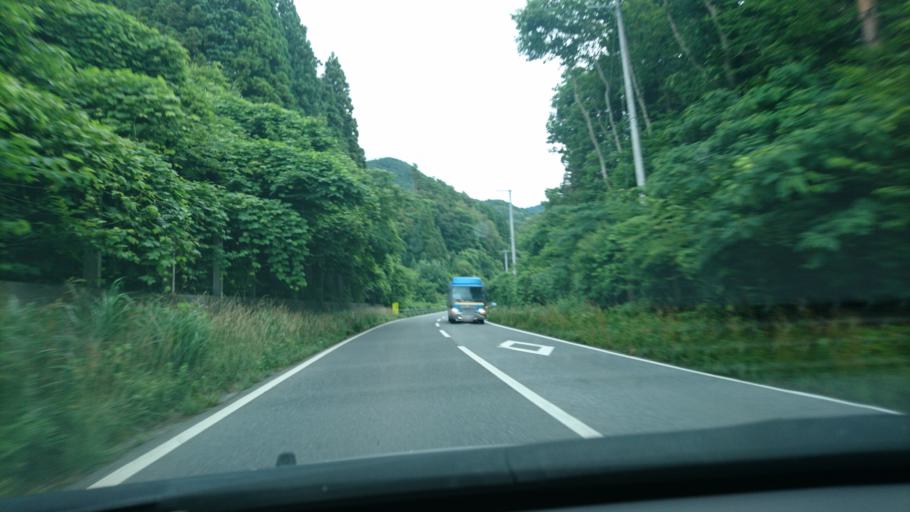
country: JP
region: Iwate
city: Kamaishi
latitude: 39.1564
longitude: 141.8408
